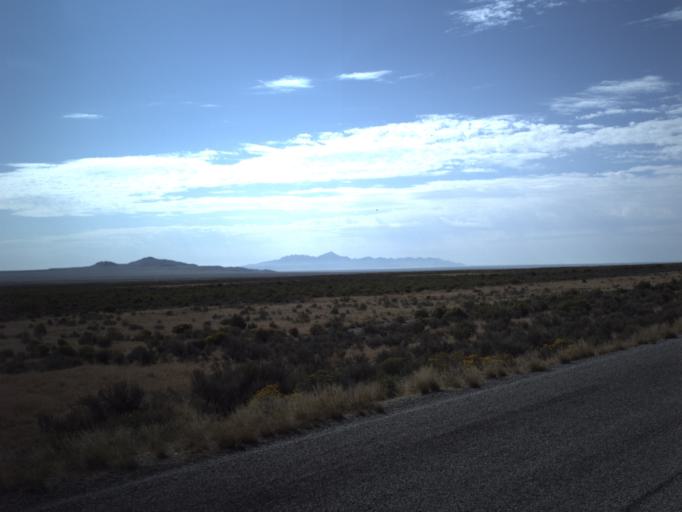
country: US
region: Utah
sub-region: Tooele County
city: Wendover
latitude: 41.5673
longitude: -113.5809
